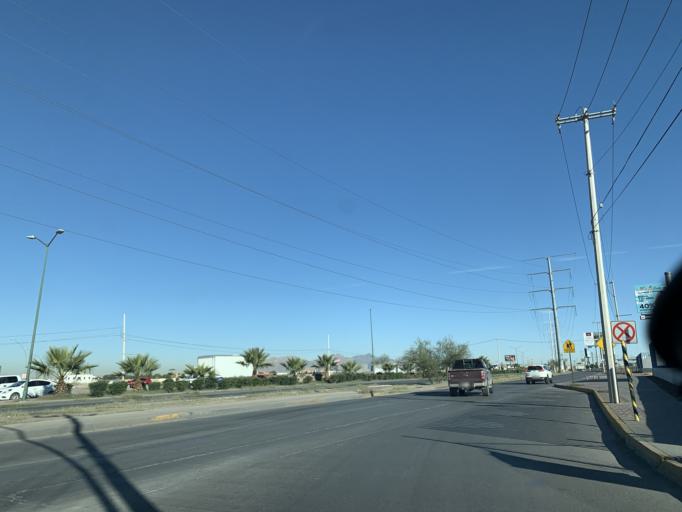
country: US
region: Texas
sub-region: El Paso County
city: Socorro
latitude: 31.6746
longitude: -106.3873
